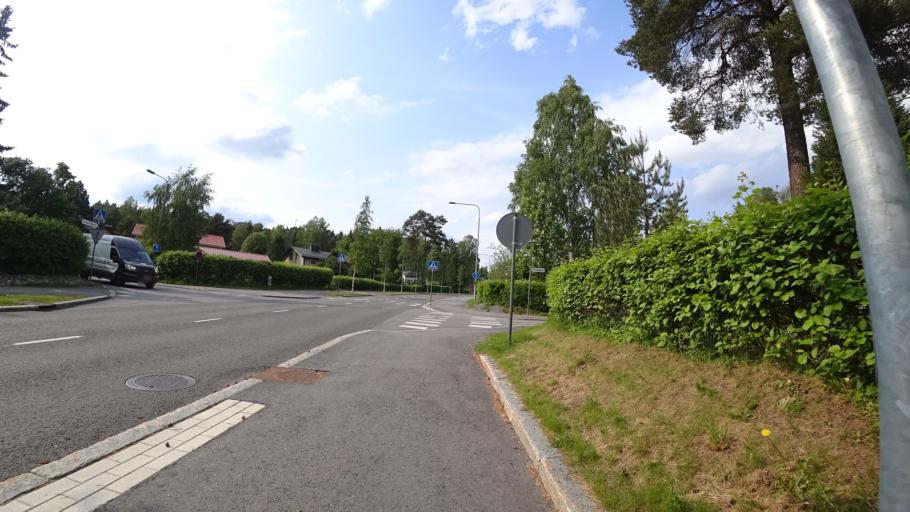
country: FI
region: Pirkanmaa
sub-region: Tampere
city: Pirkkala
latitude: 61.4993
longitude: 23.6291
